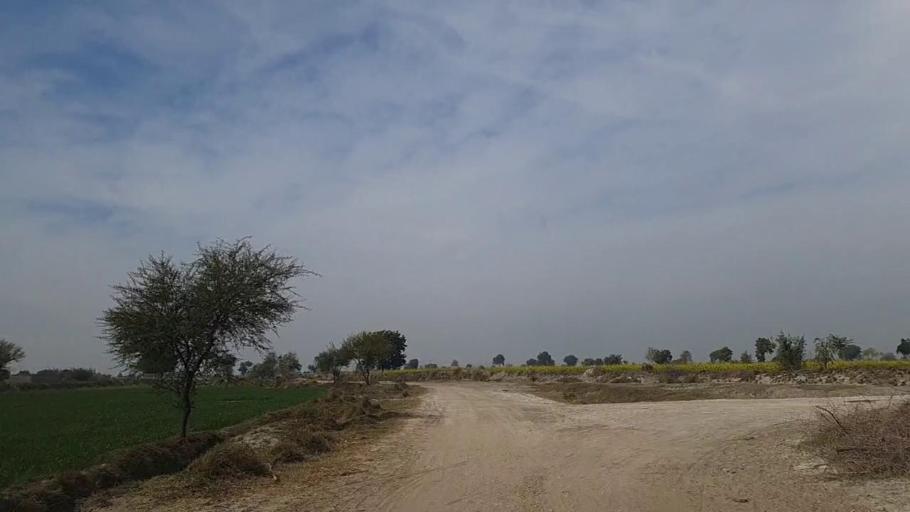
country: PK
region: Sindh
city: Nawabshah
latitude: 26.3279
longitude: 68.4223
